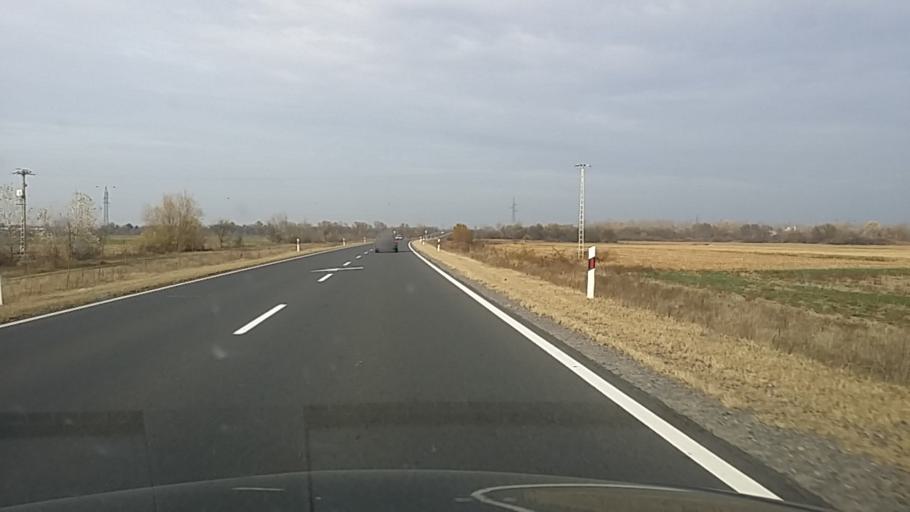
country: HU
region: Szabolcs-Szatmar-Bereg
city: Nyirpazony
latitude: 47.9385
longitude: 21.8184
